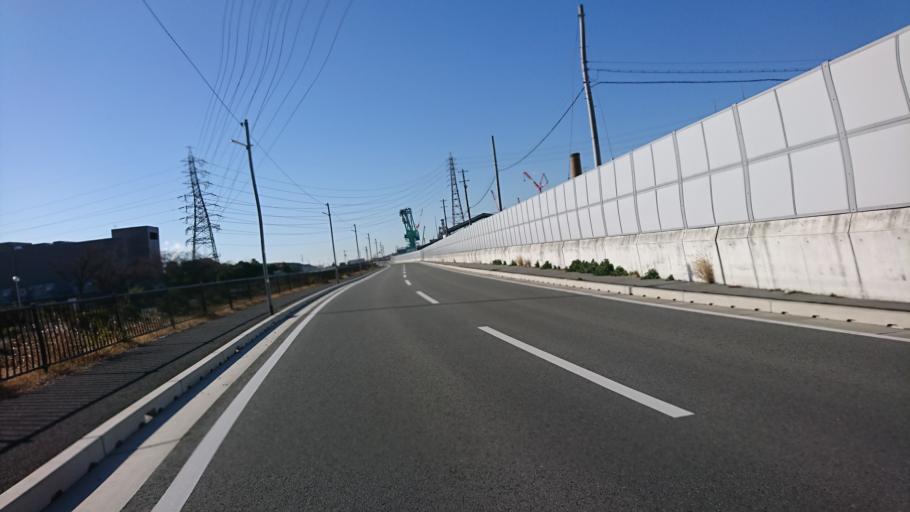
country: JP
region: Hyogo
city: Kakogawacho-honmachi
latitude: 34.7500
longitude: 134.7915
